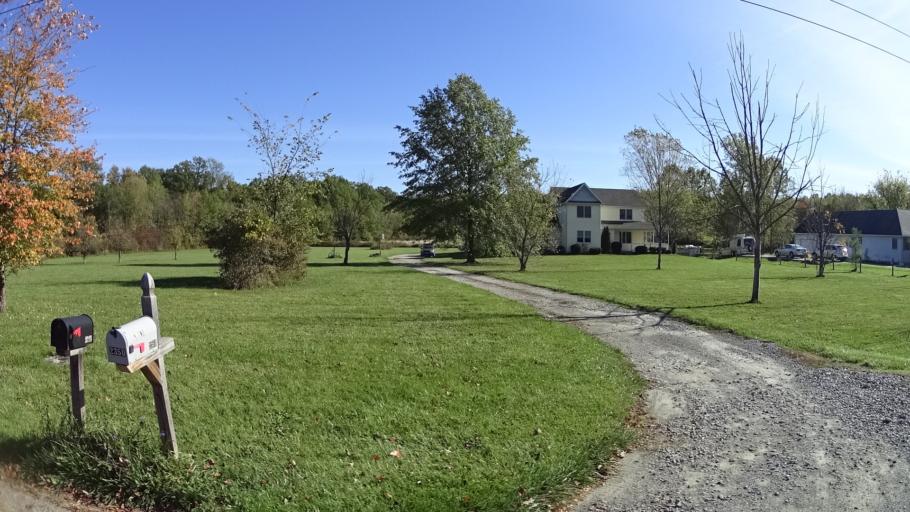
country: US
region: Ohio
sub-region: Lorain County
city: Vermilion-on-the-Lake
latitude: 41.3912
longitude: -82.3227
